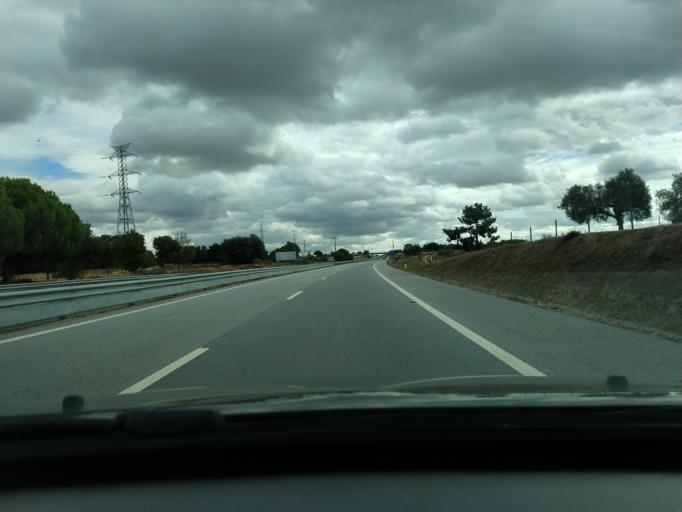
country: PT
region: Guarda
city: Alcains
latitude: 40.0048
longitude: -7.4632
